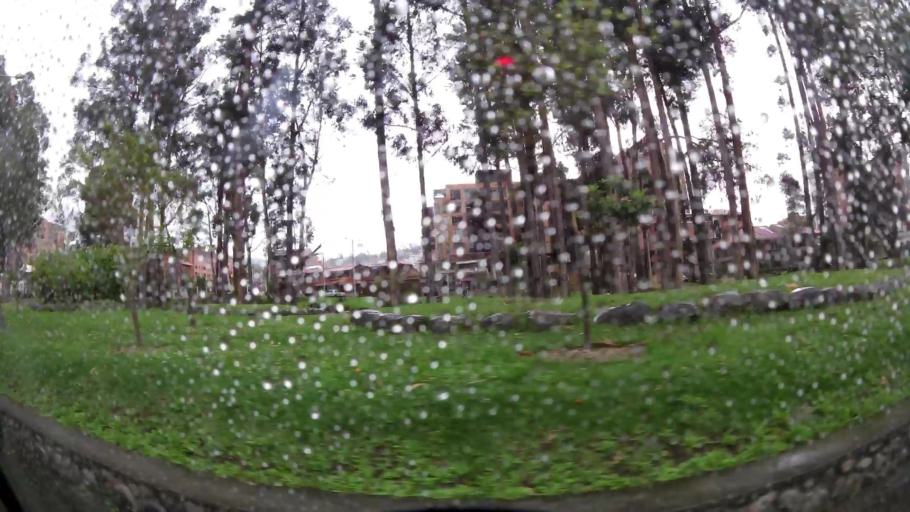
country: EC
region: Azuay
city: Cuenca
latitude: -2.8913
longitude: -79.0306
